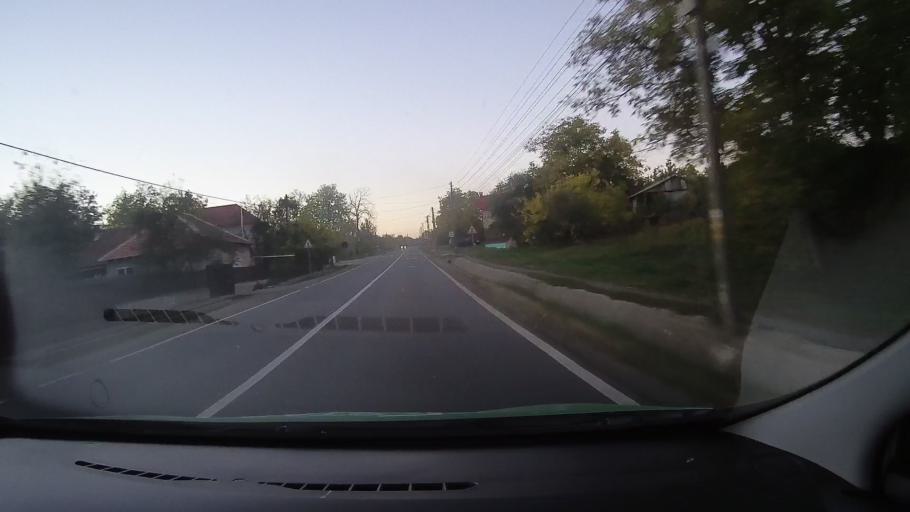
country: RO
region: Bihor
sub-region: Comuna Tarcea
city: Tarcea
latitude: 47.4618
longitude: 22.1686
